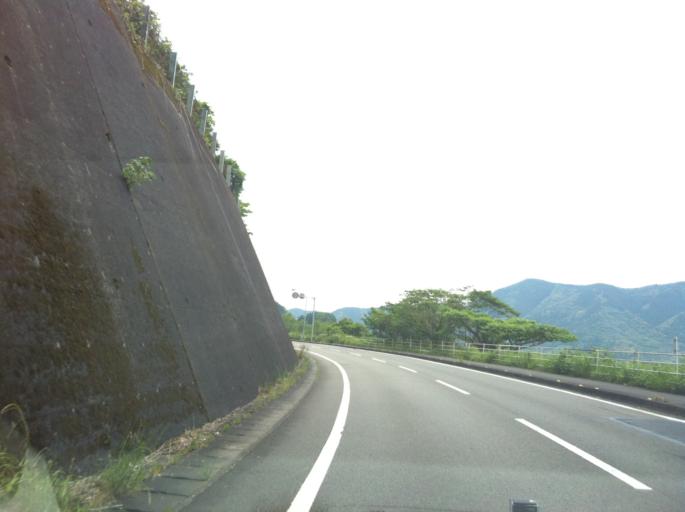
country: JP
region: Shizuoka
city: Shizuoka-shi
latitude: 35.0791
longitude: 138.3742
